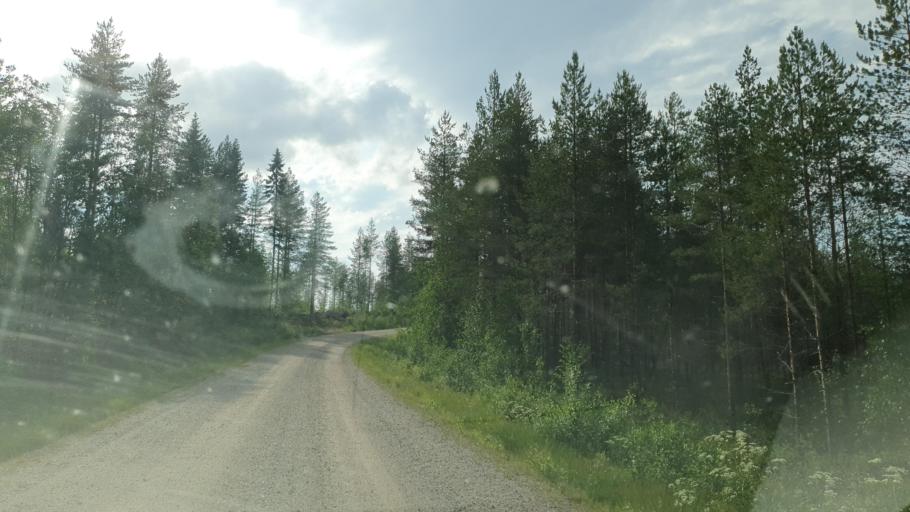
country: FI
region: Kainuu
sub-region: Kehys-Kainuu
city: Kuhmo
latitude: 64.0265
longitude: 29.8630
